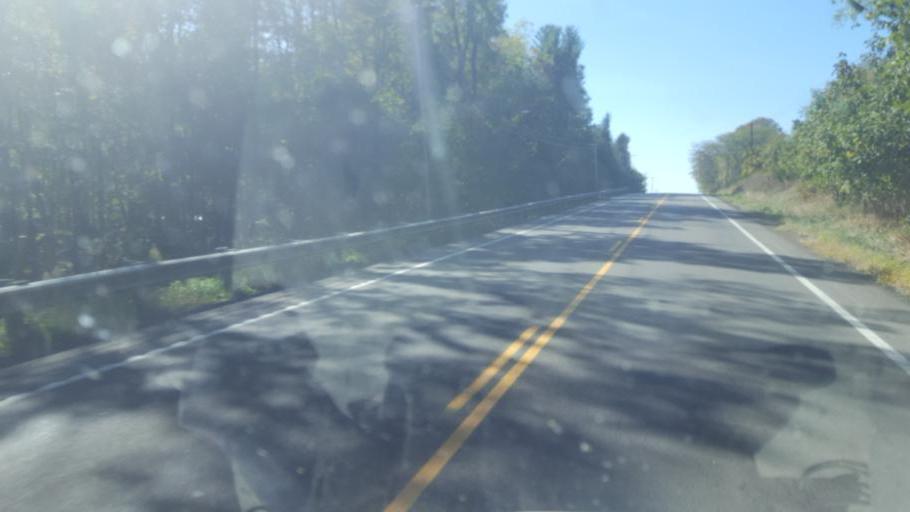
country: US
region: Ohio
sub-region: Ashland County
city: Ashland
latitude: 40.8566
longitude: -82.2038
